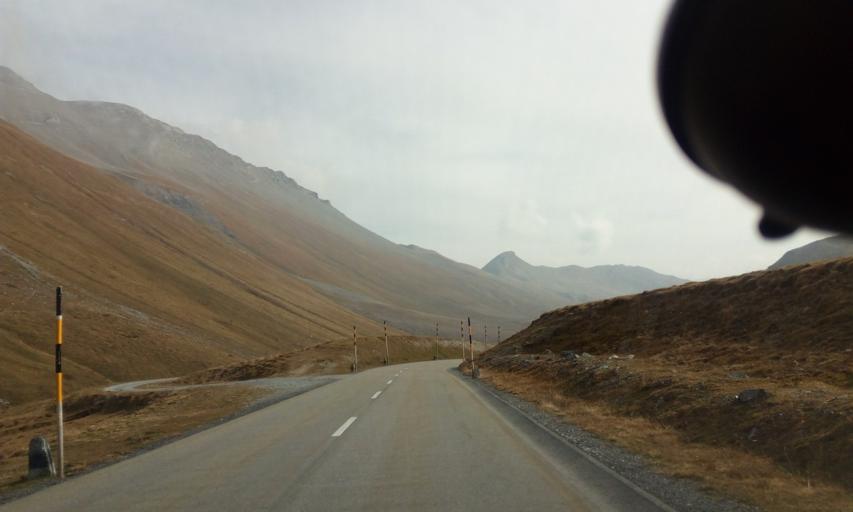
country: CH
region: Grisons
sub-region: Maloja District
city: Samedan
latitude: 46.5870
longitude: 9.8572
